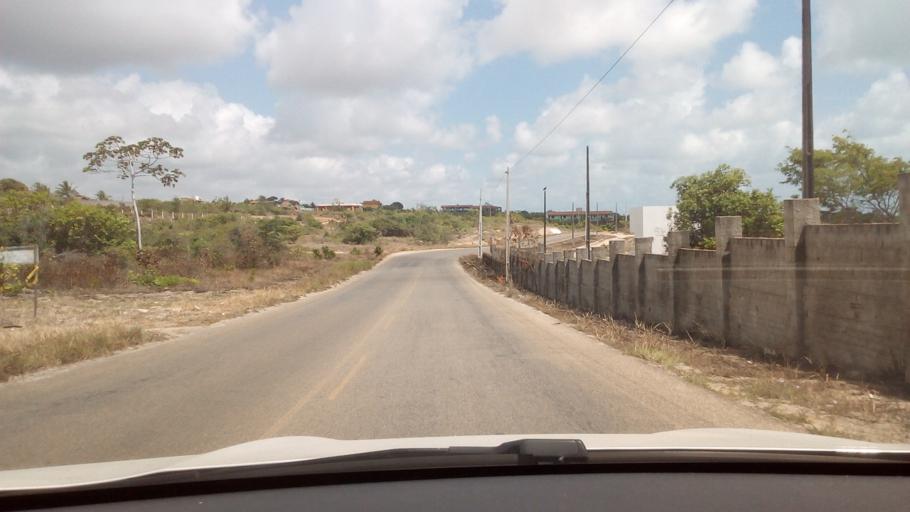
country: BR
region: Paraiba
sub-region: Conde
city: Conde
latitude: -7.3046
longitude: -34.8099
